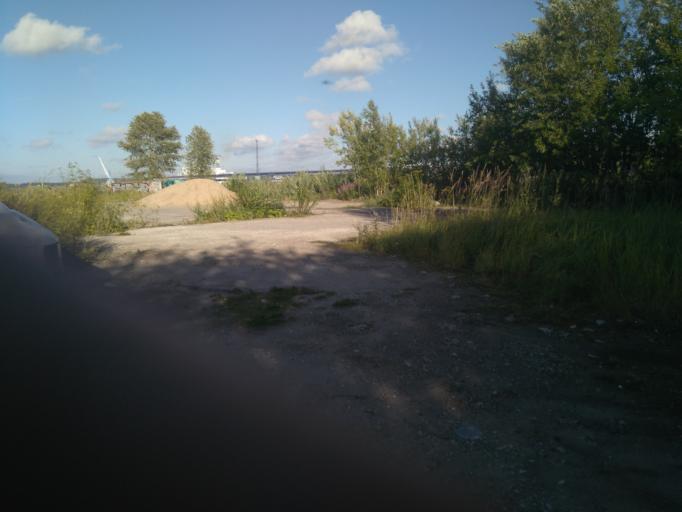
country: EE
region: Harju
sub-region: Tallinna linn
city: Tallinn
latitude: 59.4479
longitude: 24.7559
